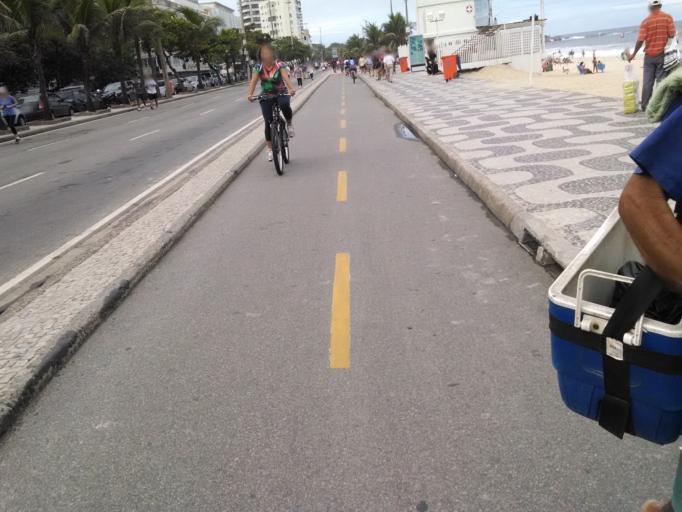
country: BR
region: Rio de Janeiro
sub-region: Rio De Janeiro
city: Rio de Janeiro
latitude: -22.9872
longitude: -43.1974
